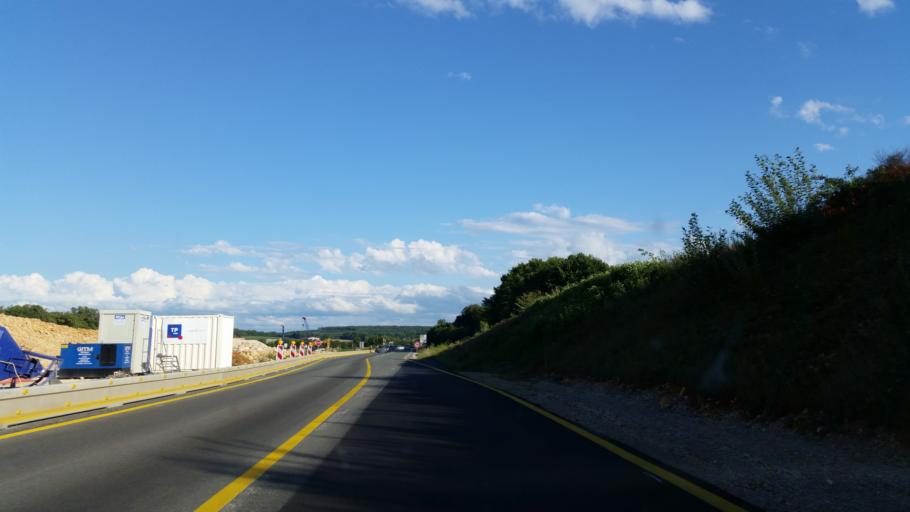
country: FR
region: Franche-Comte
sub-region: Territoire de Belfort
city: Andelnans
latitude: 47.5893
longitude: 6.8493
